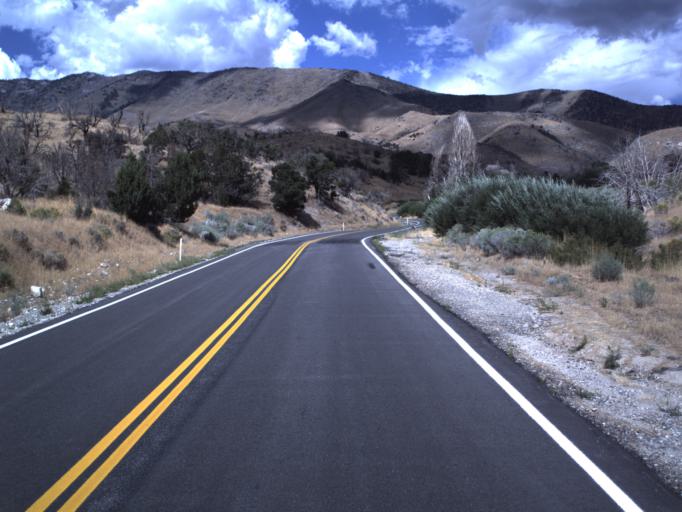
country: US
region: Utah
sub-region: Tooele County
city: Grantsville
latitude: 40.3358
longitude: -112.6141
